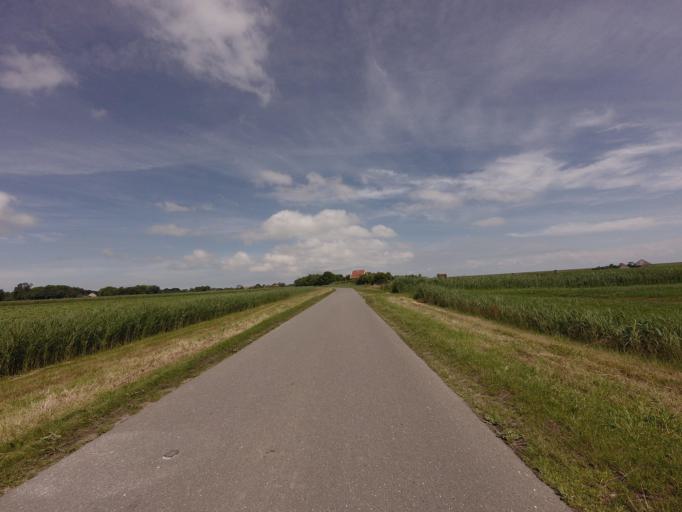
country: NL
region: North Holland
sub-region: Gemeente Texel
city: Den Burg
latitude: 53.0785
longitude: 4.8813
